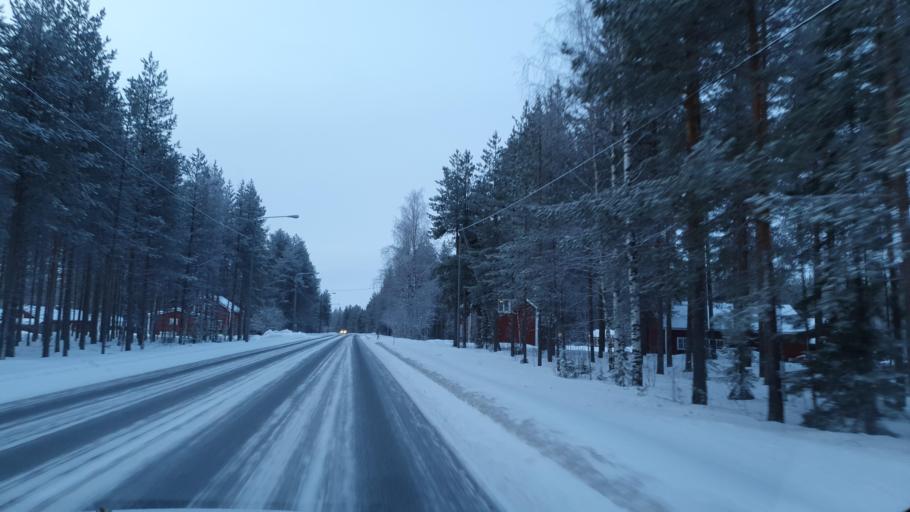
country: FI
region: Lapland
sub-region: Torniolaakso
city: Pello
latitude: 66.7168
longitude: 23.9084
